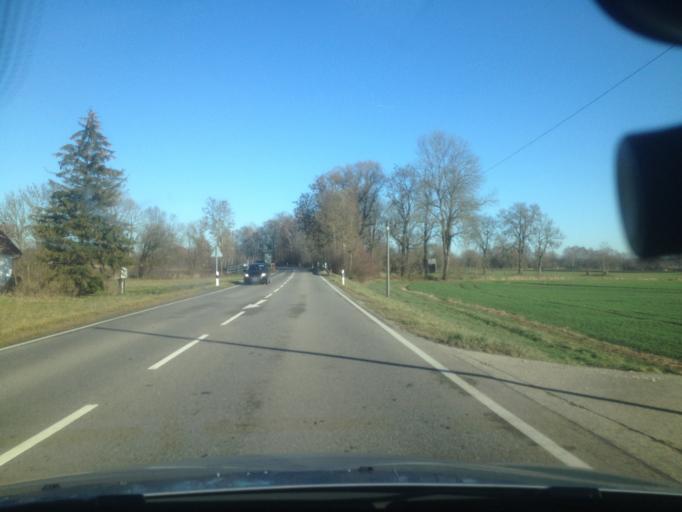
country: DE
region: Bavaria
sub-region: Upper Bavaria
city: Berglern
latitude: 48.4150
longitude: 11.9317
